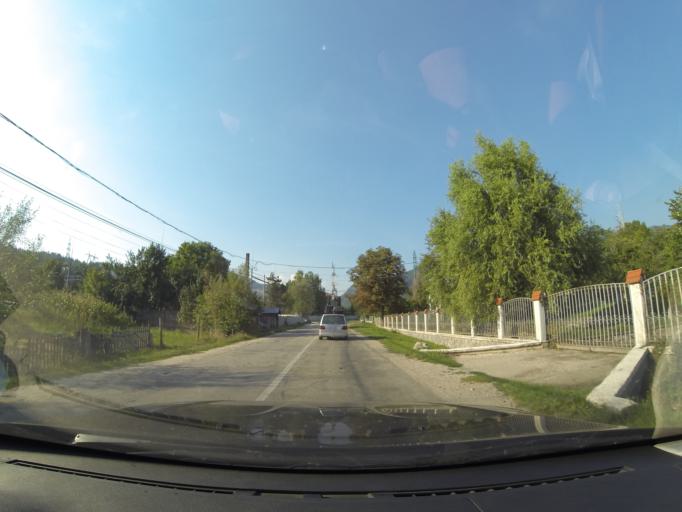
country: RO
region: Arges
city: Poenari
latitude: 45.3256
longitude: 24.6382
